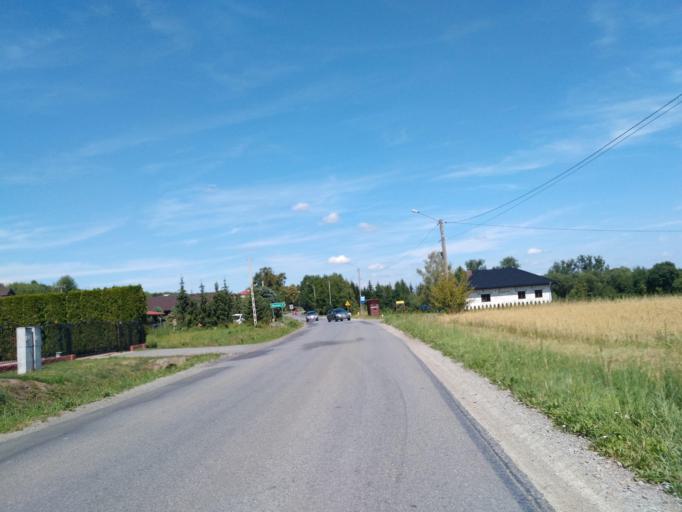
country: PL
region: Subcarpathian Voivodeship
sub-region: Powiat sanocki
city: Bukowsko
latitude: 49.5201
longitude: 22.1011
